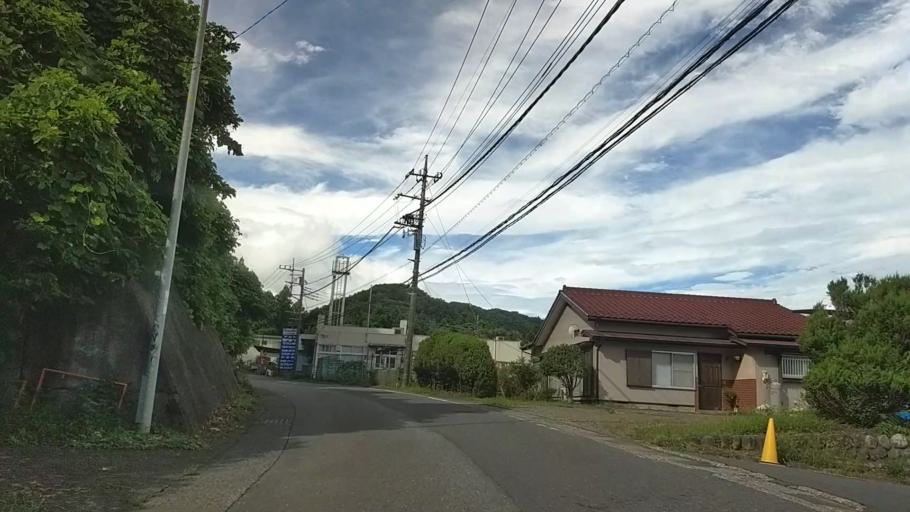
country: JP
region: Yamanashi
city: Uenohara
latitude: 35.6040
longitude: 139.1537
